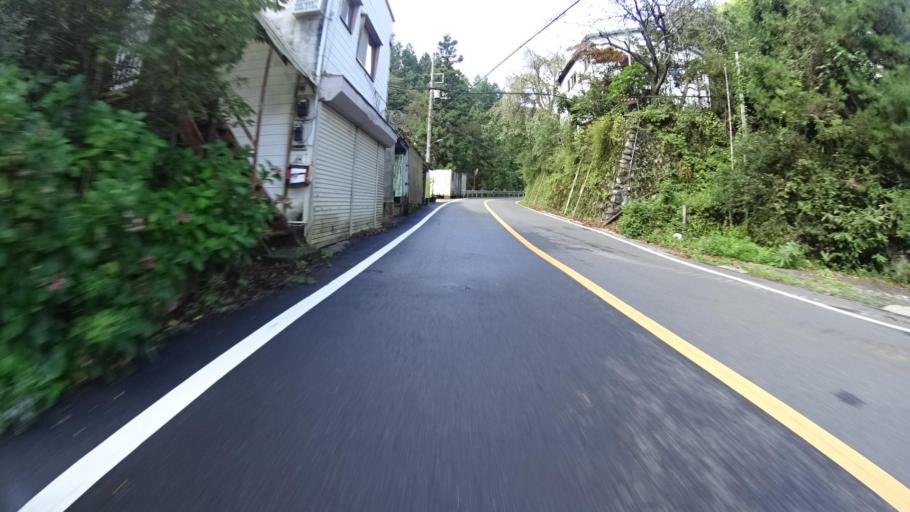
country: JP
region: Tokyo
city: Itsukaichi
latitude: 35.7315
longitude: 139.1100
